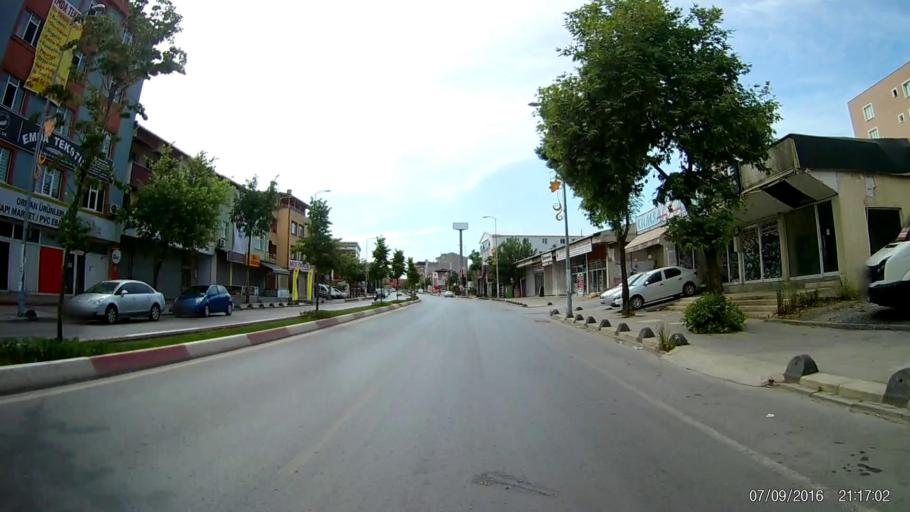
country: TR
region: Istanbul
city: Sultanbeyli
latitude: 40.9632
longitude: 29.2863
